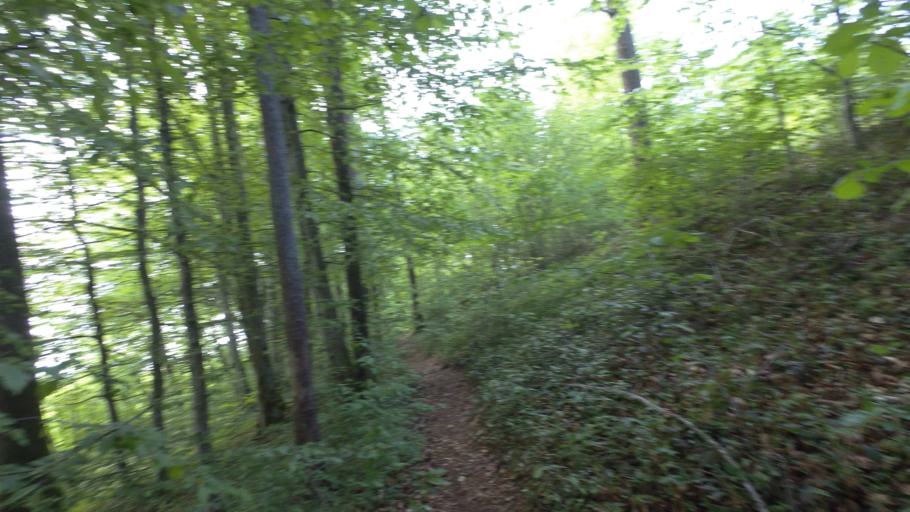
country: DE
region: Bavaria
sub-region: Upper Bavaria
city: Grabenstatt
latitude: 47.8440
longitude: 12.5659
